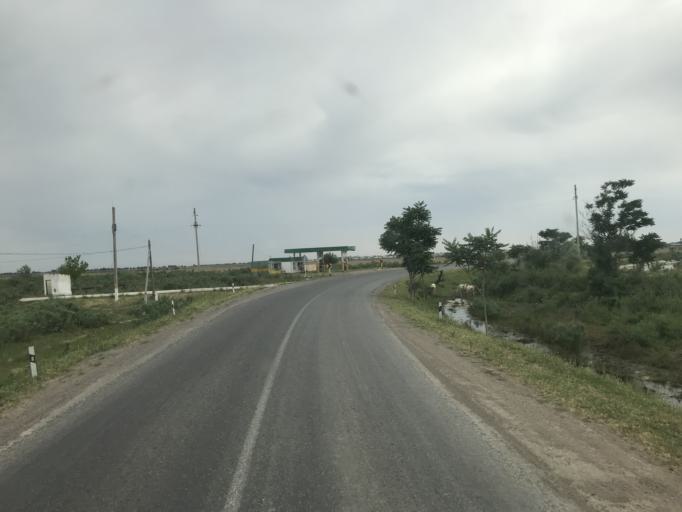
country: KZ
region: Ongtustik Qazaqstan
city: Asykata
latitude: 40.9107
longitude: 68.3924
